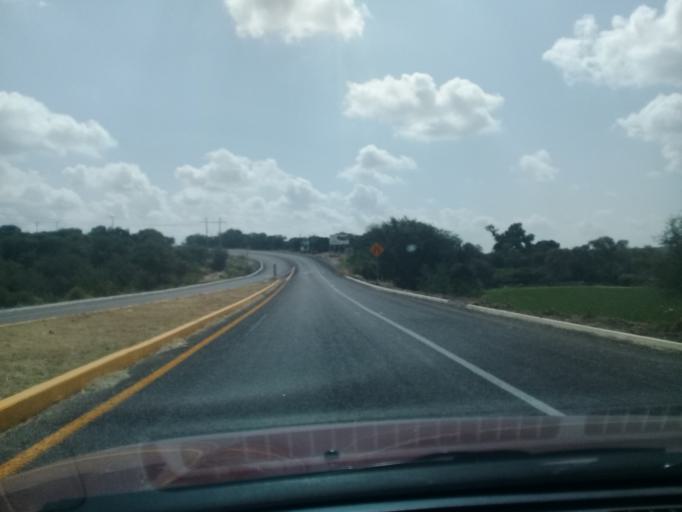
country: MX
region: Aguascalientes
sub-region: Aguascalientes
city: Penuelas (El Cienegal)
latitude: 21.7690
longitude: -102.3585
